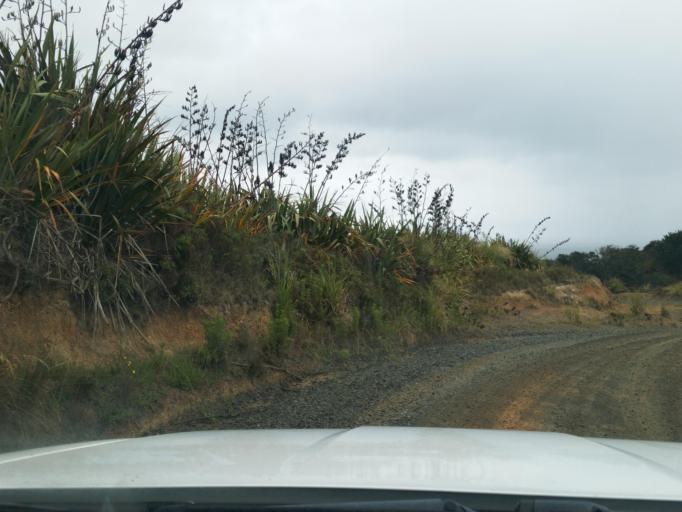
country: NZ
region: Northland
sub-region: Kaipara District
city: Dargaville
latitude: -36.0007
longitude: 173.7946
